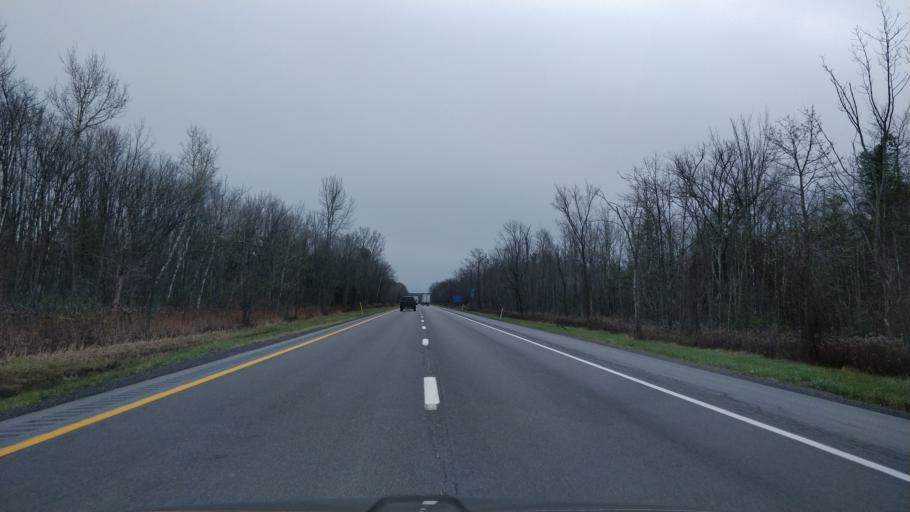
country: US
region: New York
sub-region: Jefferson County
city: Adams
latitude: 43.7910
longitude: -76.0423
